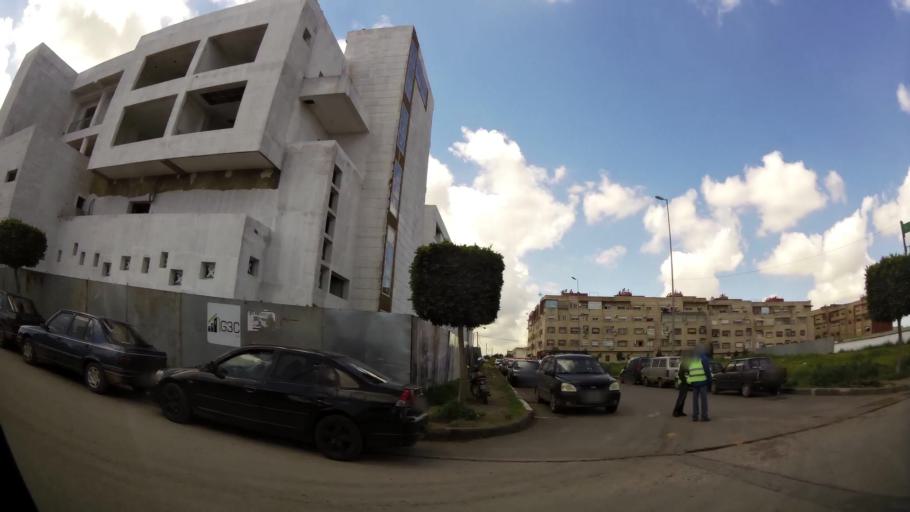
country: MA
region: Grand Casablanca
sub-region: Casablanca
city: Casablanca
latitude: 33.5403
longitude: -7.5581
